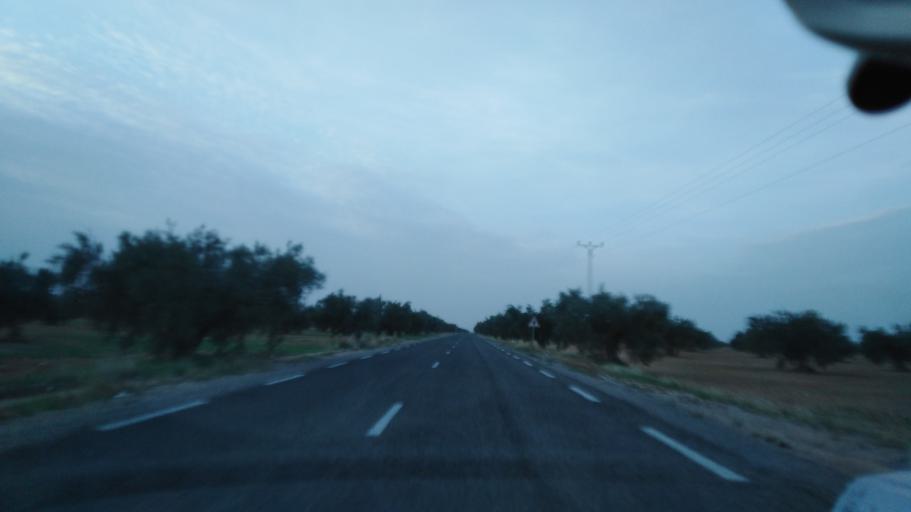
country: TN
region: Safaqis
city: Bi'r `Ali Bin Khalifah
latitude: 34.9092
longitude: 10.3877
